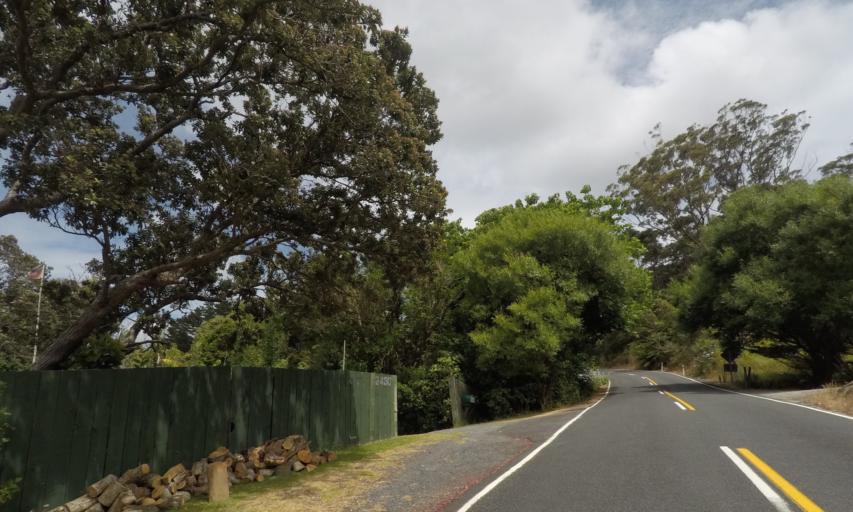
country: NZ
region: Northland
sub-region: Whangarei
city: Ruakaka
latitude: -35.8311
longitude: 174.5320
